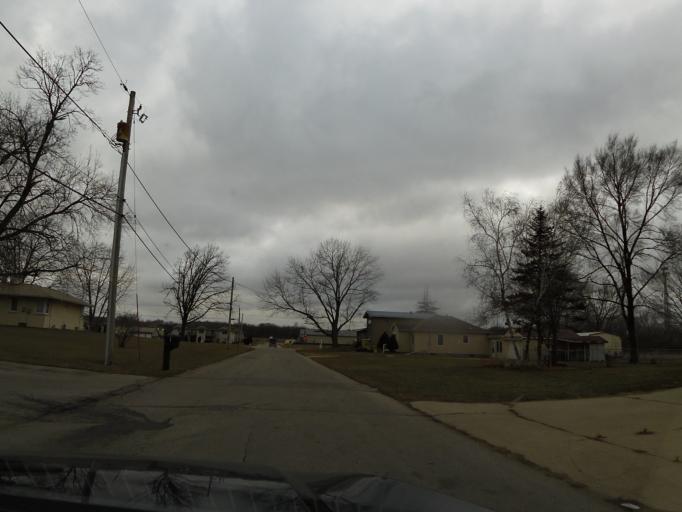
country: US
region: Iowa
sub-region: Black Hawk County
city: Evansdale
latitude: 42.4646
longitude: -92.2964
